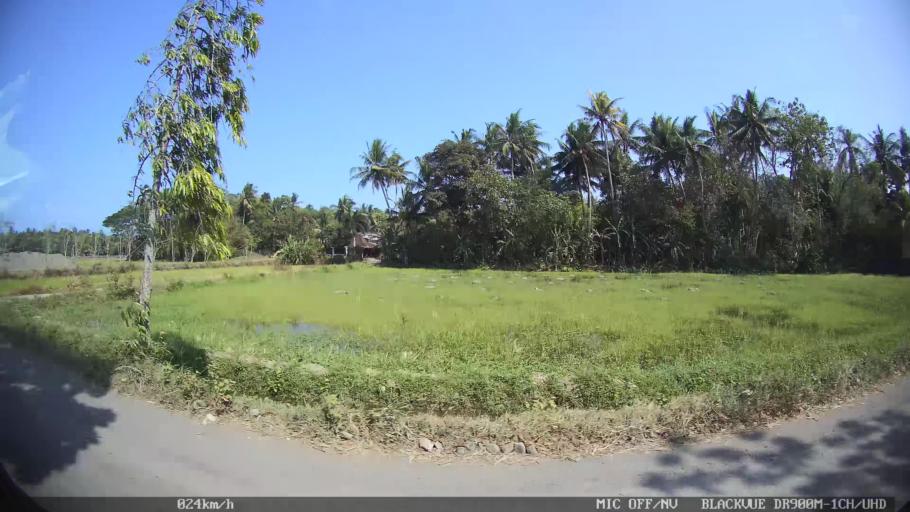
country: ID
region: Daerah Istimewa Yogyakarta
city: Srandakan
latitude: -7.9541
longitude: 110.2178
